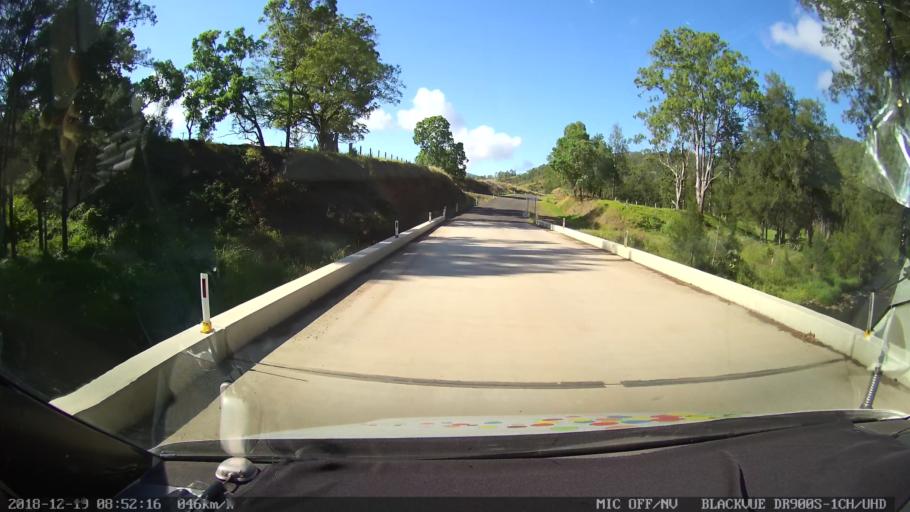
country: AU
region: New South Wales
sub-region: Kyogle
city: Kyogle
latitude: -28.3939
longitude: 152.9779
